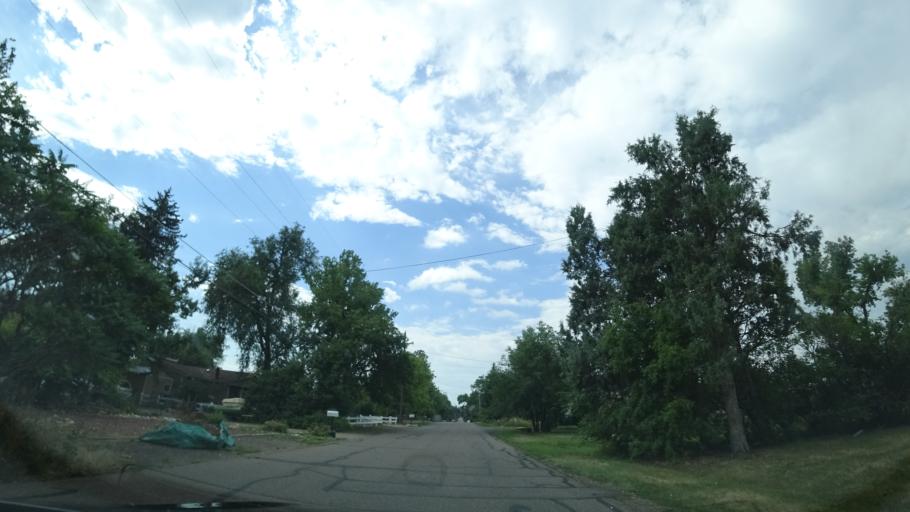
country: US
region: Colorado
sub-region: Jefferson County
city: Lakewood
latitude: 39.7230
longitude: -105.0651
